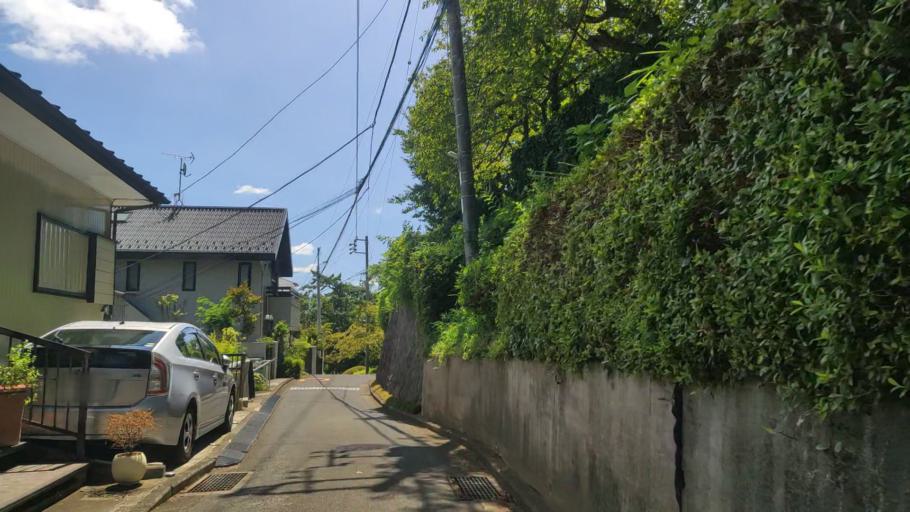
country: JP
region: Kanagawa
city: Yokohama
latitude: 35.5240
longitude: 139.6285
